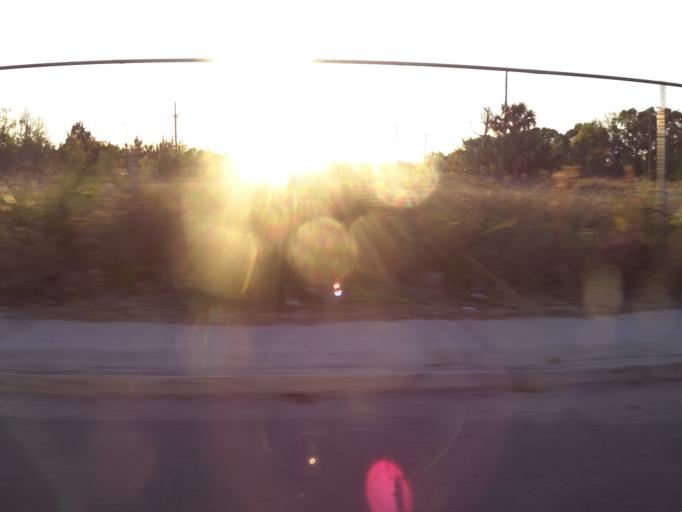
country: US
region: Florida
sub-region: Duval County
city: Jacksonville
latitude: 30.3300
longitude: -81.7056
